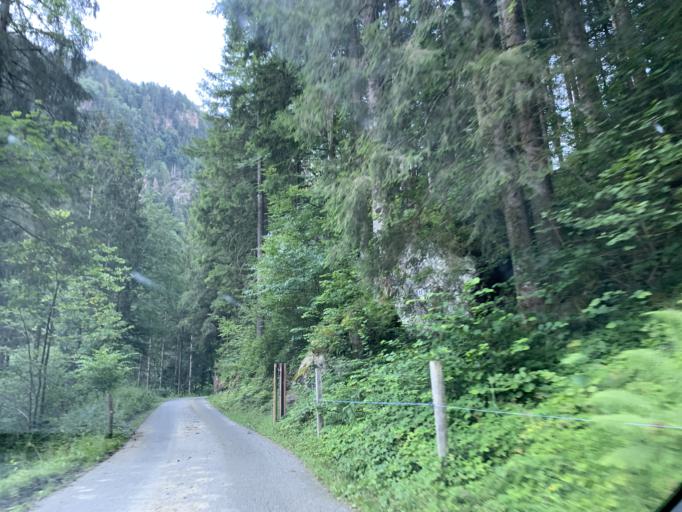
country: CH
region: Saint Gallen
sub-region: Wahlkreis Sarganserland
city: Quarten
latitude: 47.0962
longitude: 9.2095
